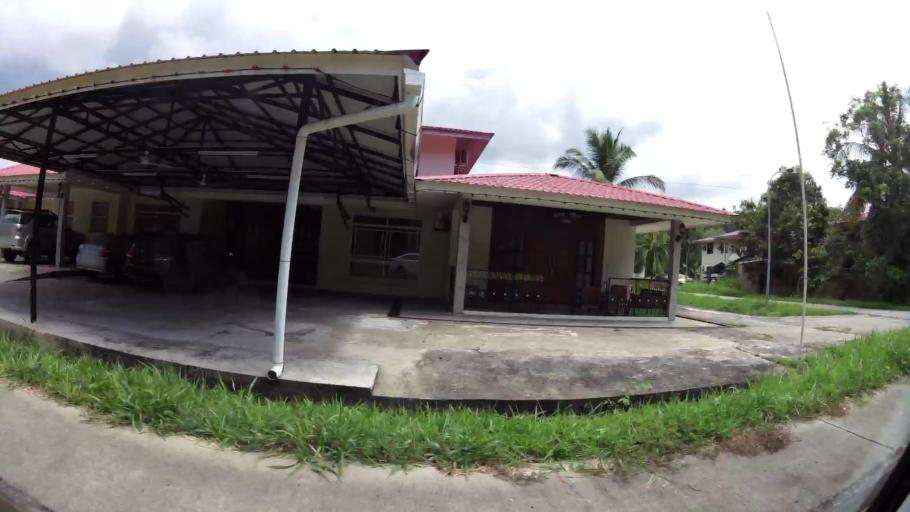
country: BN
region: Brunei and Muara
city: Bandar Seri Begawan
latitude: 4.9836
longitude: 114.9332
